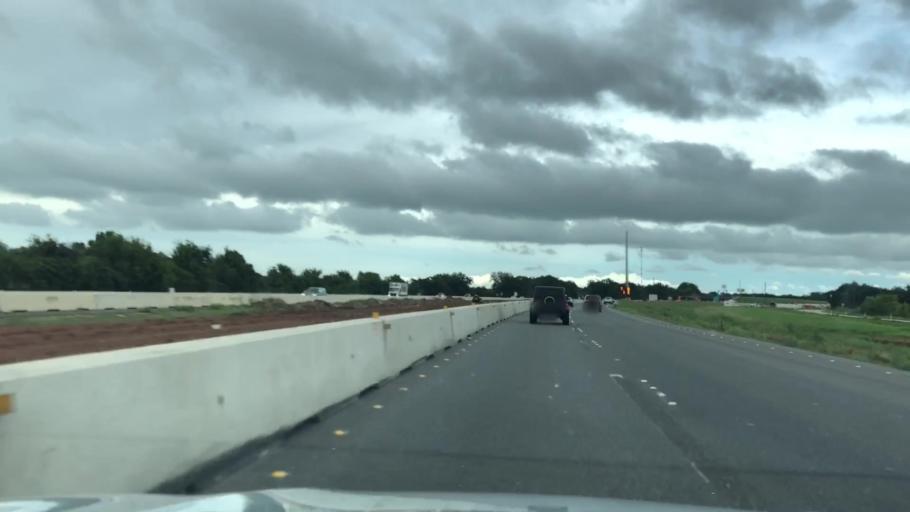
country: US
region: Texas
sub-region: Waller County
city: Brookshire
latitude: 29.7810
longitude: -95.9943
